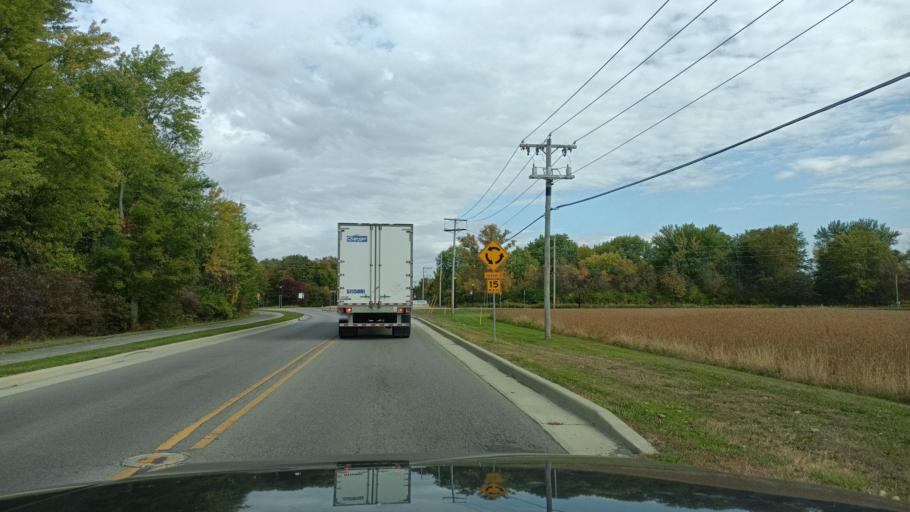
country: US
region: Indiana
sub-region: Delaware County
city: Yorktown
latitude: 40.2042
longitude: -85.4618
